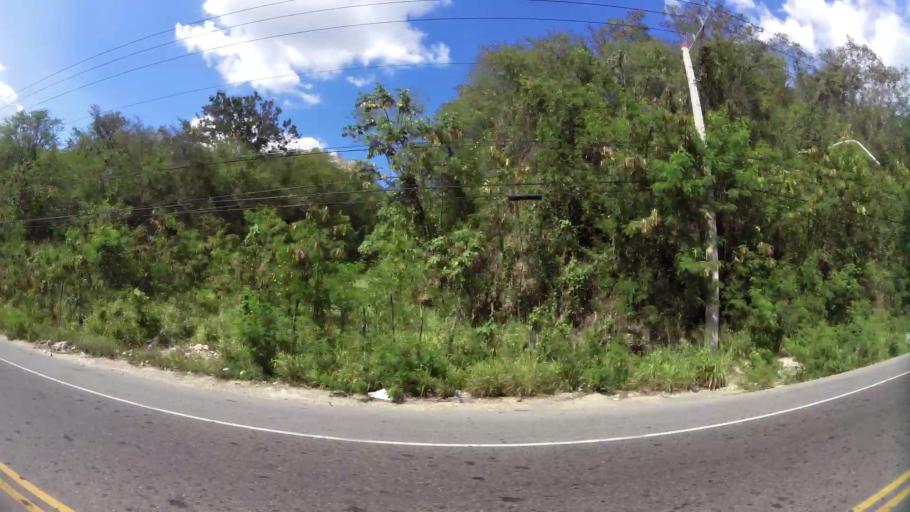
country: DO
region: San Cristobal
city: Bajos de Haina
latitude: 18.4266
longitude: -70.0434
